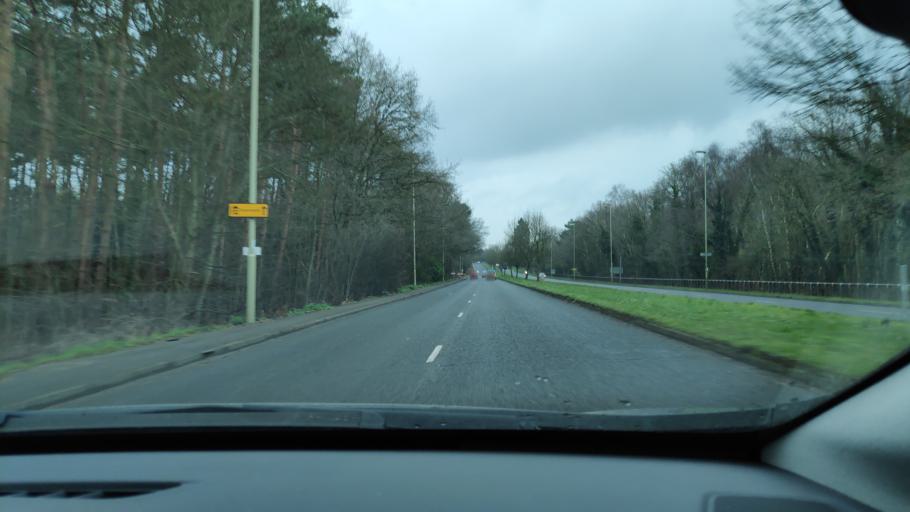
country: GB
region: England
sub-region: Hampshire
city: Aldershot
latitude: 51.2640
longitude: -0.7648
